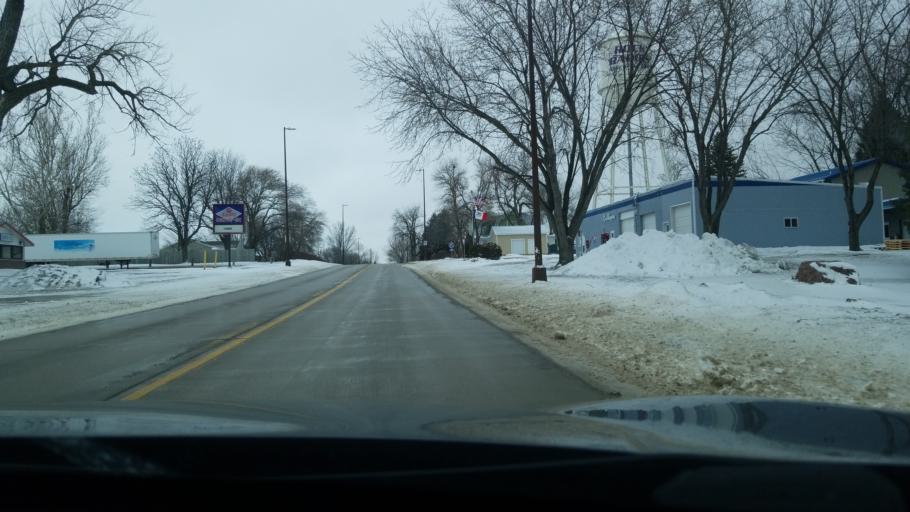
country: US
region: Iowa
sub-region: Lyon County
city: Rock Rapids
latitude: 43.4244
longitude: -96.1757
